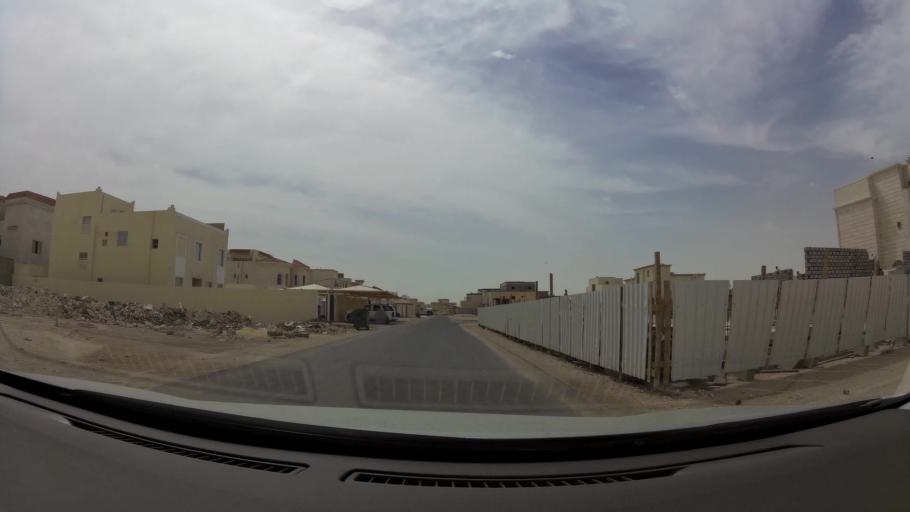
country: QA
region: Baladiyat ad Dawhah
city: Doha
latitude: 25.2119
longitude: 51.4687
